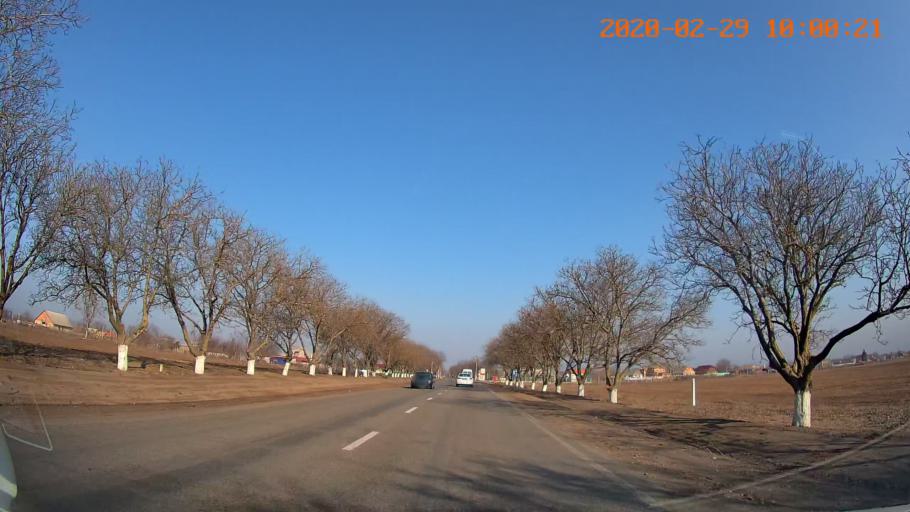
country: MD
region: Telenesti
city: Slobozia
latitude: 46.7673
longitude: 29.6864
